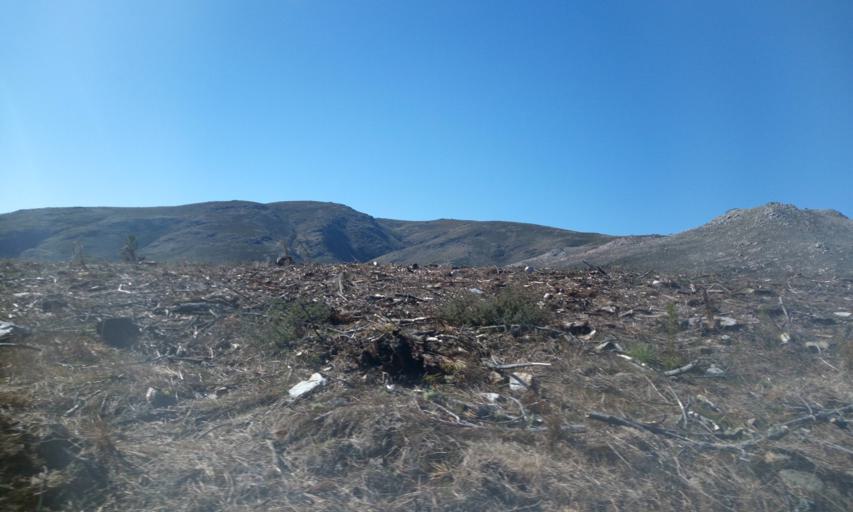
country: PT
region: Guarda
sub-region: Manteigas
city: Manteigas
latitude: 40.4771
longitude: -7.5074
